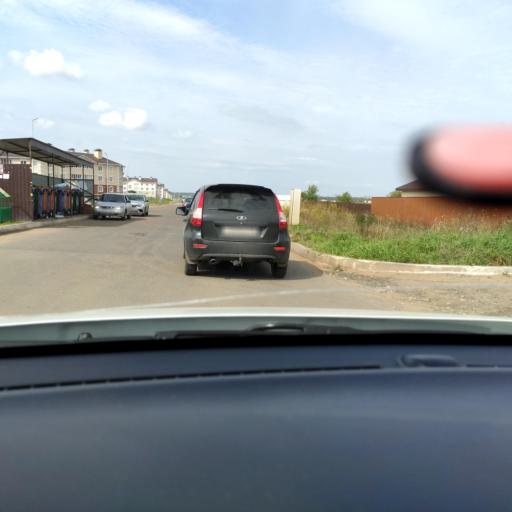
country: RU
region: Tatarstan
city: Stolbishchi
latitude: 55.7087
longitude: 49.3426
